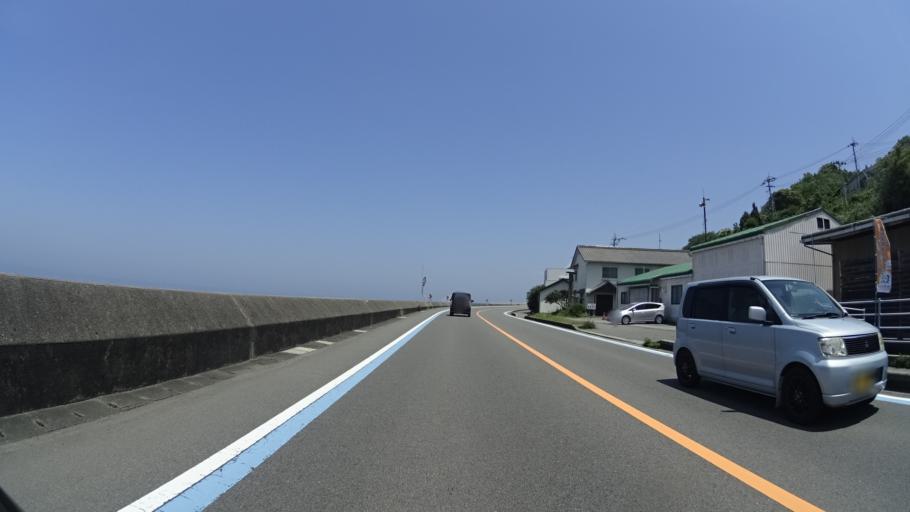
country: JP
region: Ehime
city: Iyo
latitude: 33.6570
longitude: 132.5910
